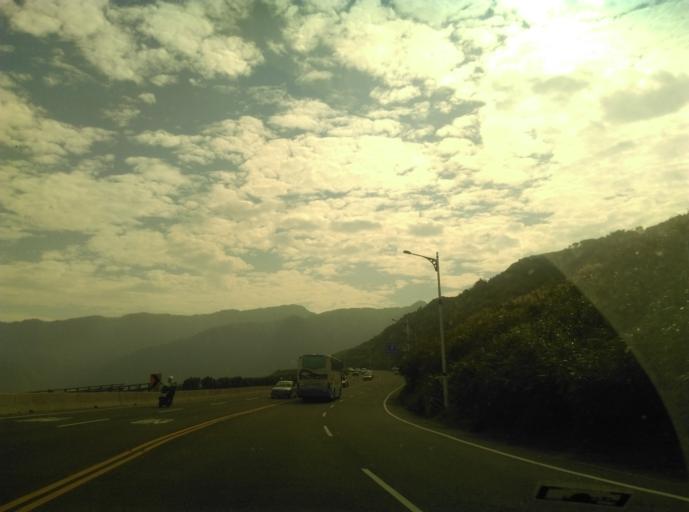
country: TW
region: Taiwan
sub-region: Keelung
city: Keelung
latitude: 25.1738
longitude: 121.7083
